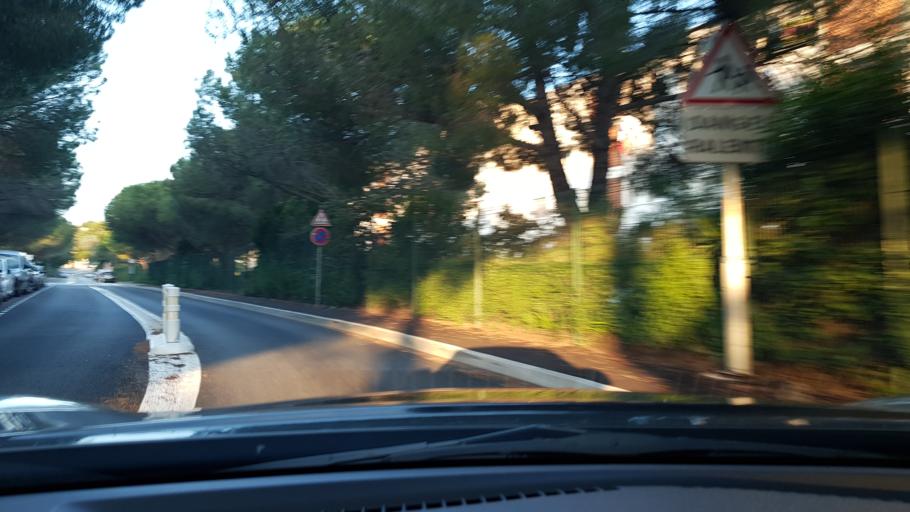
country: FR
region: Provence-Alpes-Cote d'Azur
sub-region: Departement des Alpes-Maritimes
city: Vallauris
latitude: 43.5866
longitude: 7.0452
